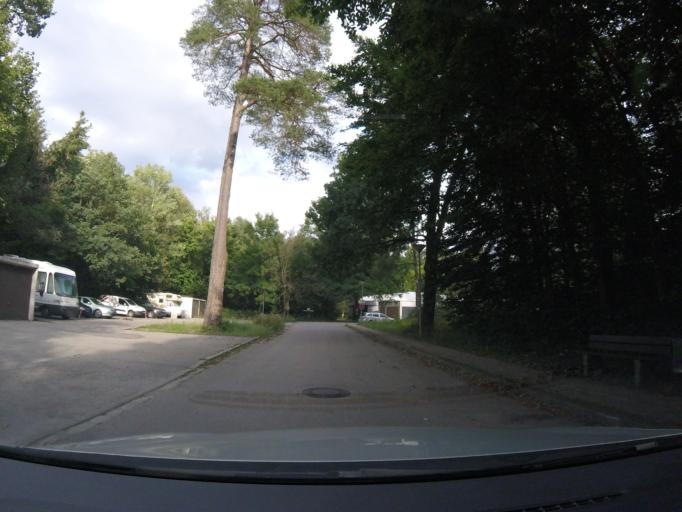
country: DE
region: Bavaria
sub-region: Upper Bavaria
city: Hohenbrunn
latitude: 48.0636
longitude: 11.7021
